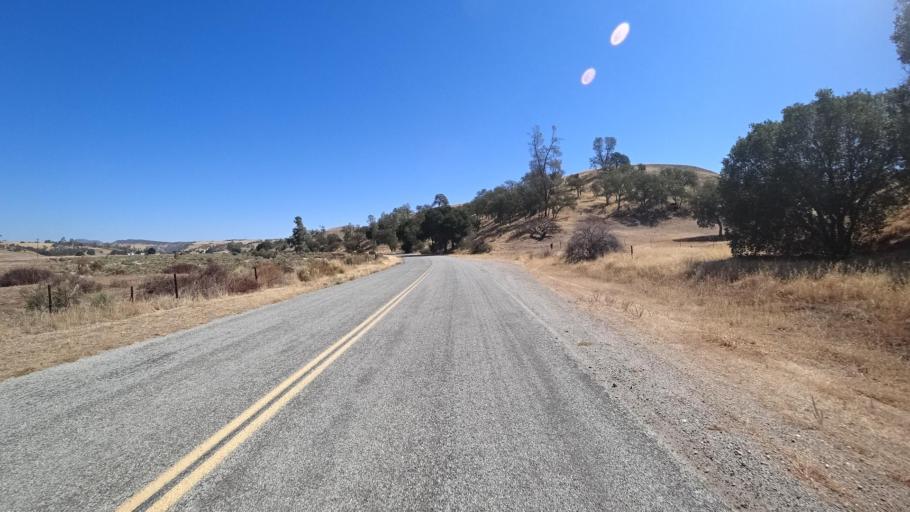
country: US
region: California
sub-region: San Luis Obispo County
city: San Miguel
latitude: 35.8372
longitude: -120.6267
